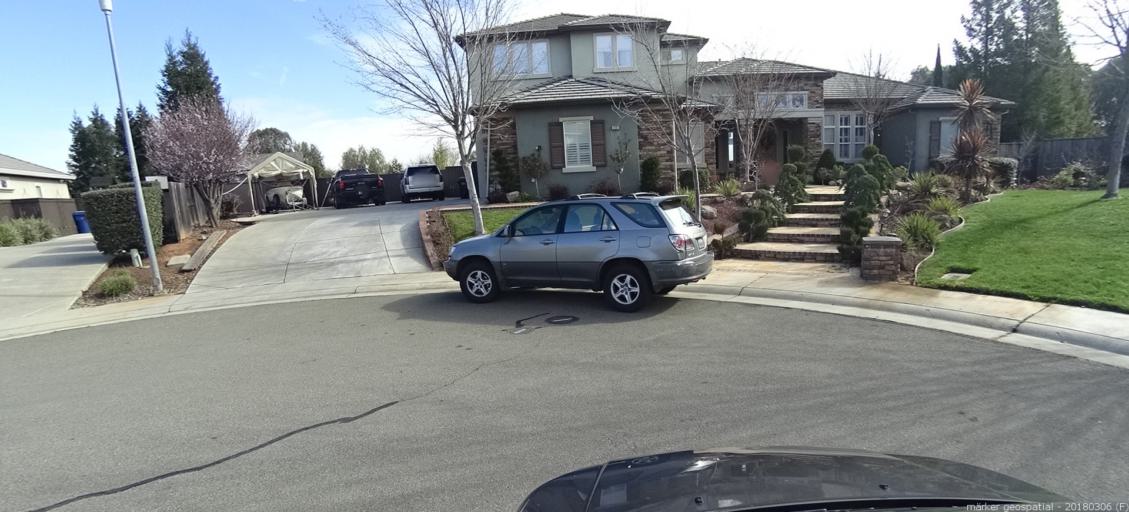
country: US
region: California
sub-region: Sacramento County
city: Vineyard
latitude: 38.4744
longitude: -121.3075
